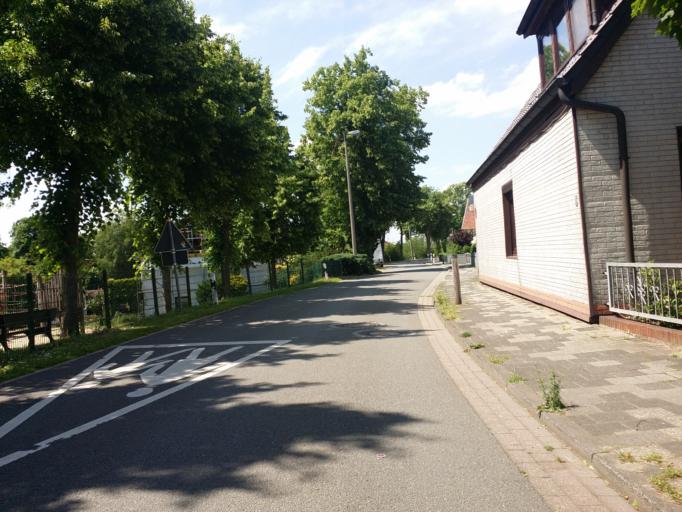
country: DE
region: Lower Saxony
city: Ritterhude
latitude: 53.1114
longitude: 8.7082
